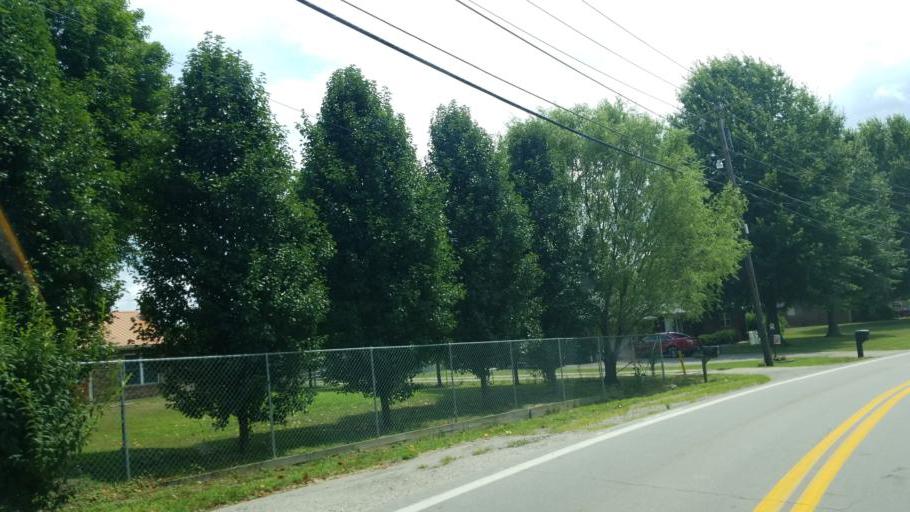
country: US
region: West Virginia
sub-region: Kanawha County
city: Nitro
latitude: 38.4431
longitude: -81.8543
